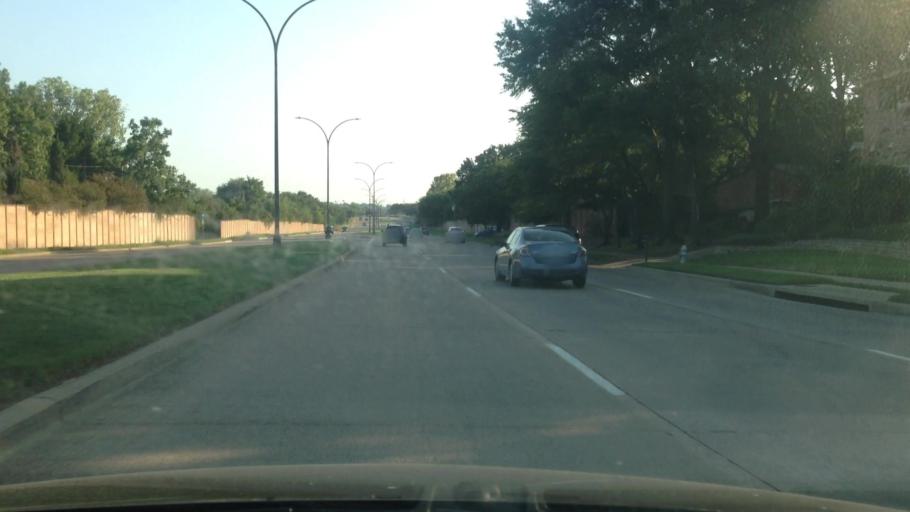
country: US
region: Texas
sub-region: Tarrant County
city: Dalworthington Gardens
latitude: 32.6880
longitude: -97.1925
